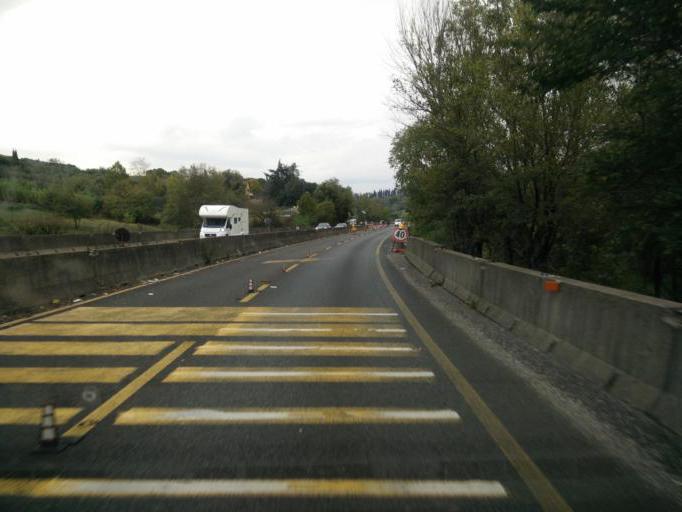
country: IT
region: Tuscany
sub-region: Province of Florence
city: Tavarnuzze
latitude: 43.7137
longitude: 11.2165
